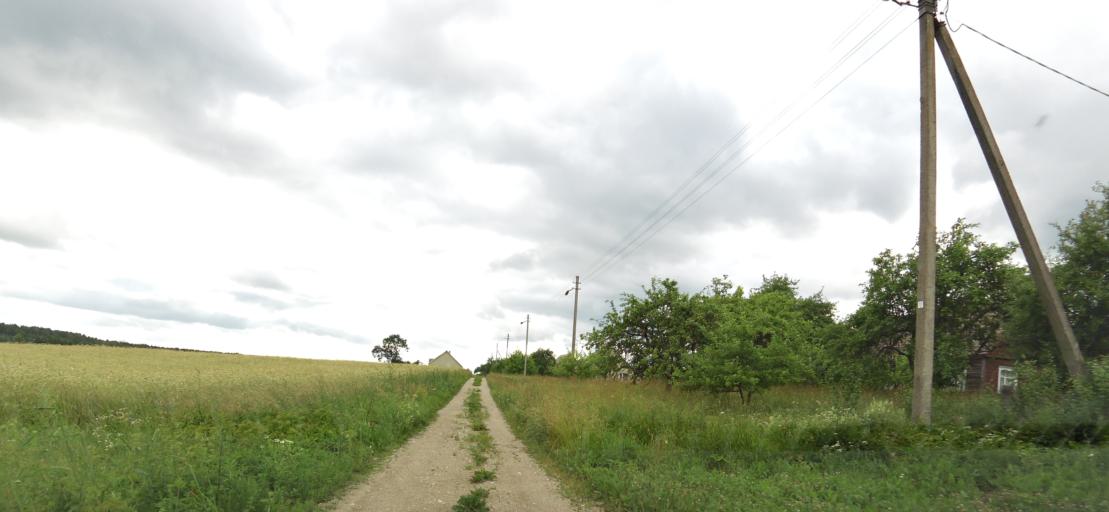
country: LT
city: Obeliai
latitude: 56.0701
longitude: 25.1088
